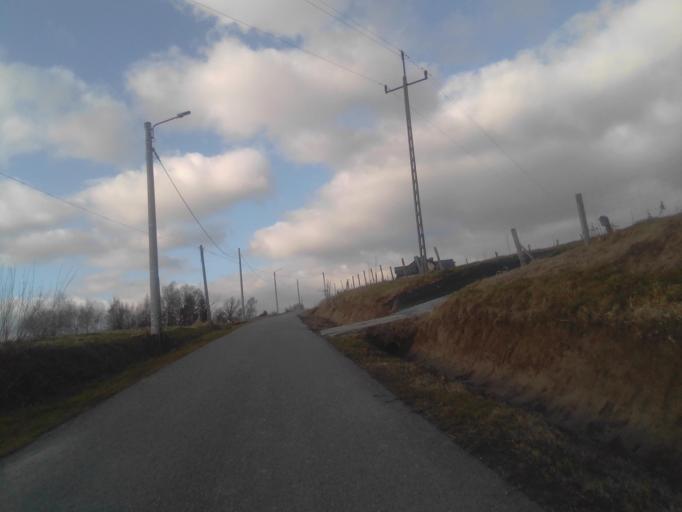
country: PL
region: Subcarpathian Voivodeship
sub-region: Powiat strzyzowski
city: Babica
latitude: 49.9375
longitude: 21.8986
